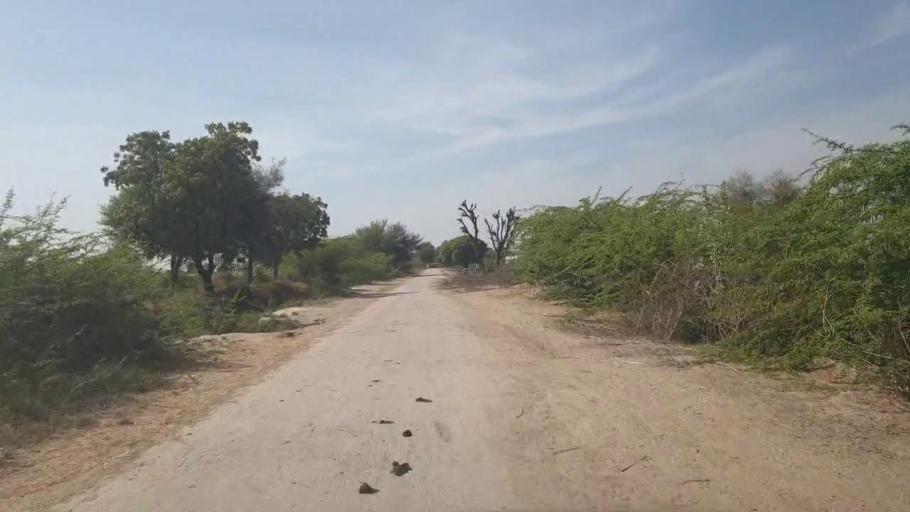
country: PK
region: Sindh
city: Kunri
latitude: 25.1850
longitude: 69.6769
